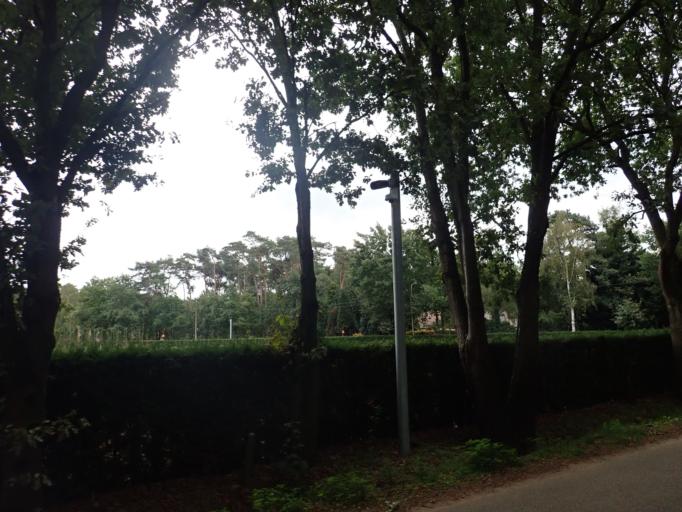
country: BE
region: Flanders
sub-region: Provincie Antwerpen
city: Beerse
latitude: 51.2930
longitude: 4.8375
